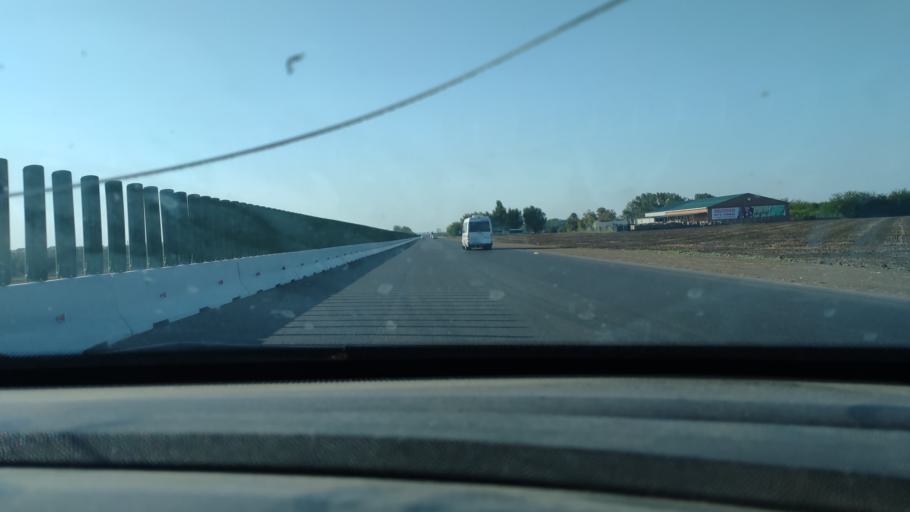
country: RU
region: Krasnodarskiy
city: Medvedovskaya
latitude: 45.4730
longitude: 38.9749
